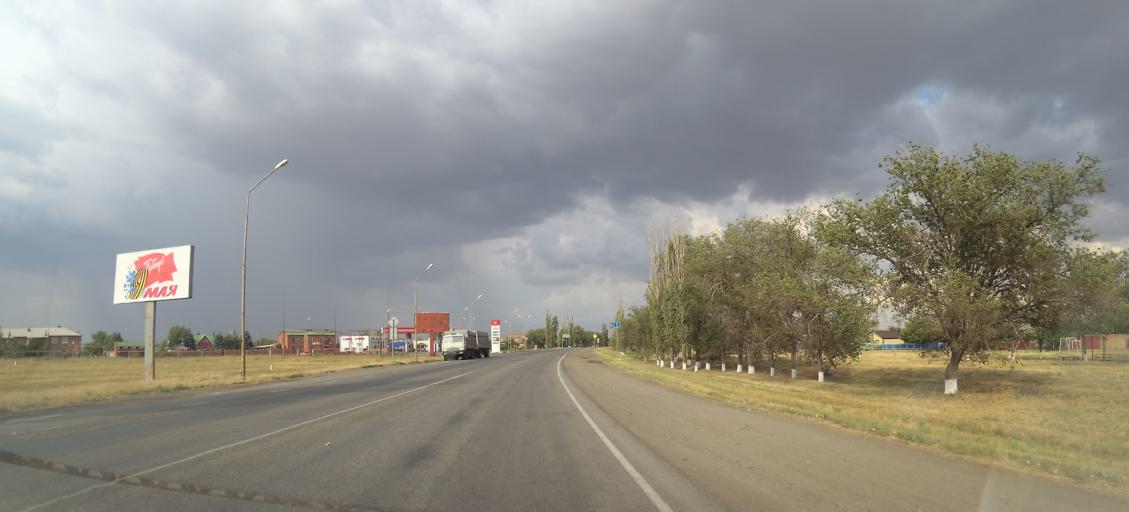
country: RU
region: Rostov
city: Zimovniki
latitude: 47.1442
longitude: 42.4415
